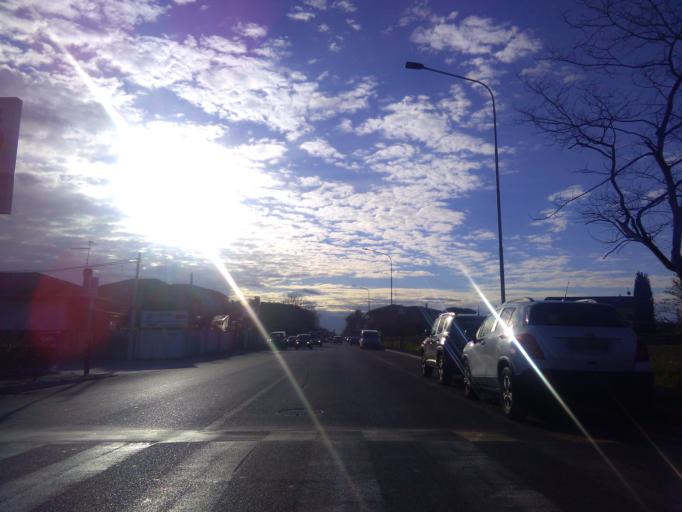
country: IT
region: Tuscany
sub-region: Provincia di Massa-Carrara
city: Marina di Carrara
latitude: 44.0532
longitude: 10.0429
